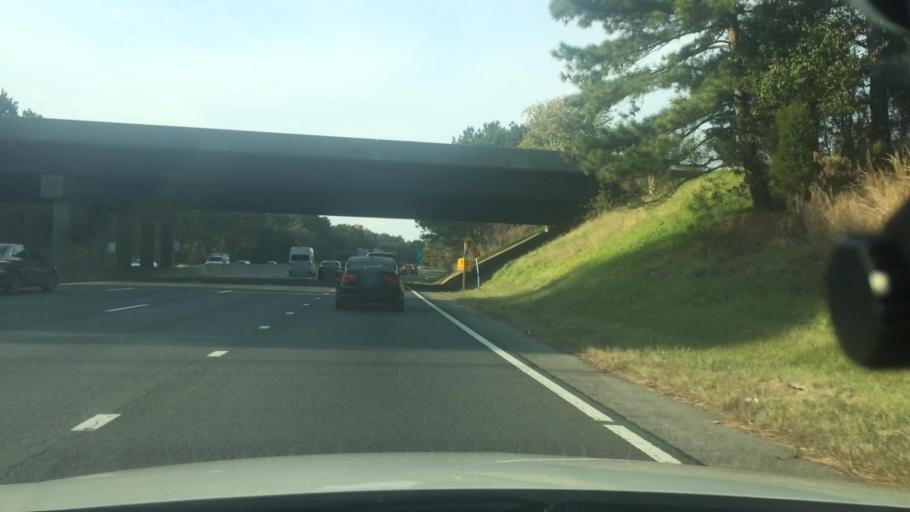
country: US
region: North Carolina
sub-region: Orange County
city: Chapel Hill
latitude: 35.9129
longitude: -78.9816
